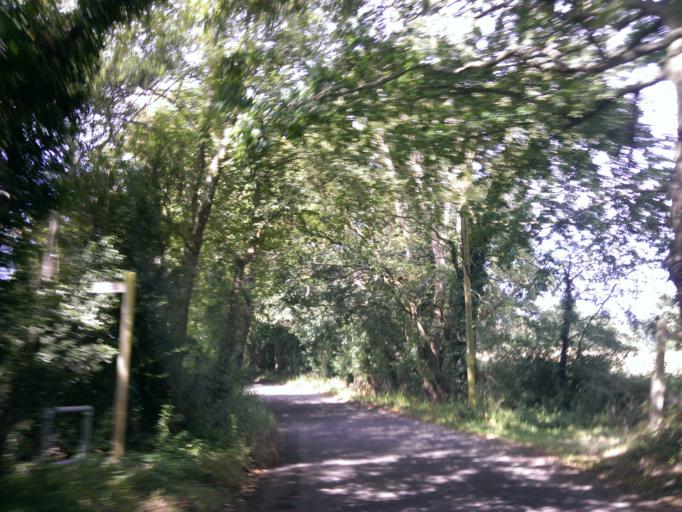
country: GB
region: England
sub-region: Essex
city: Sible Hedingham
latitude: 51.9627
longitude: 0.6284
